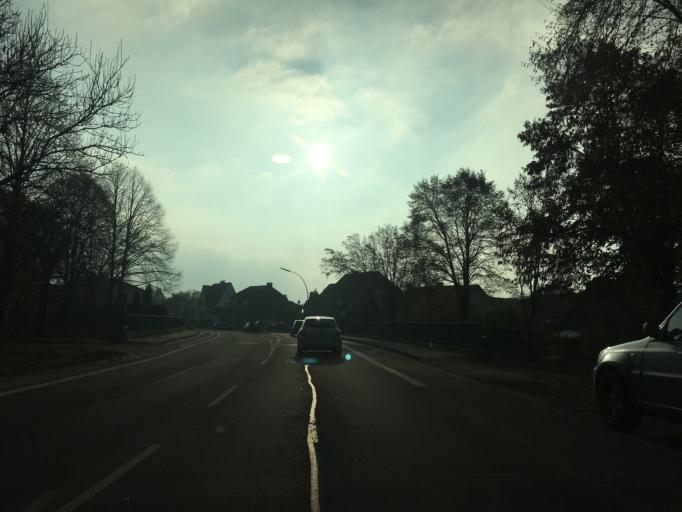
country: DE
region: North Rhine-Westphalia
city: Ludinghausen
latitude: 51.7814
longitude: 7.4489
